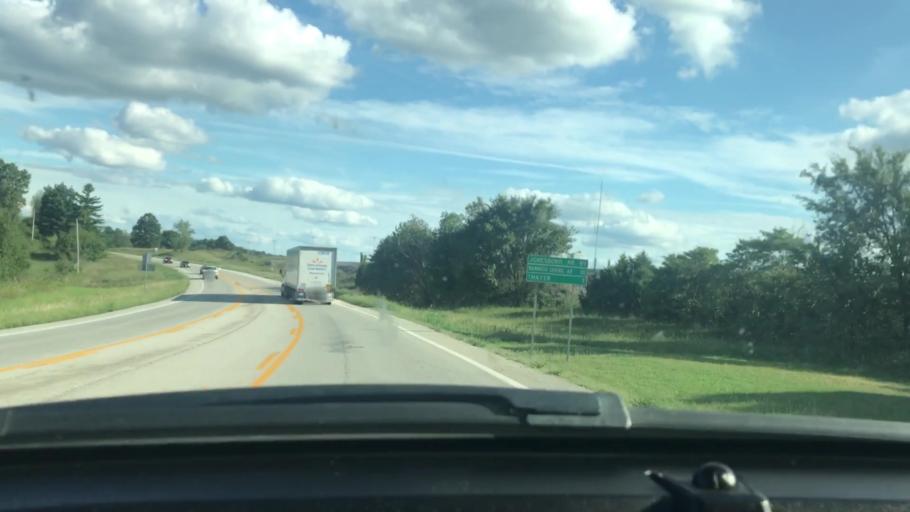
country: US
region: Missouri
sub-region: Oregon County
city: Thayer
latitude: 36.5920
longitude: -91.6435
